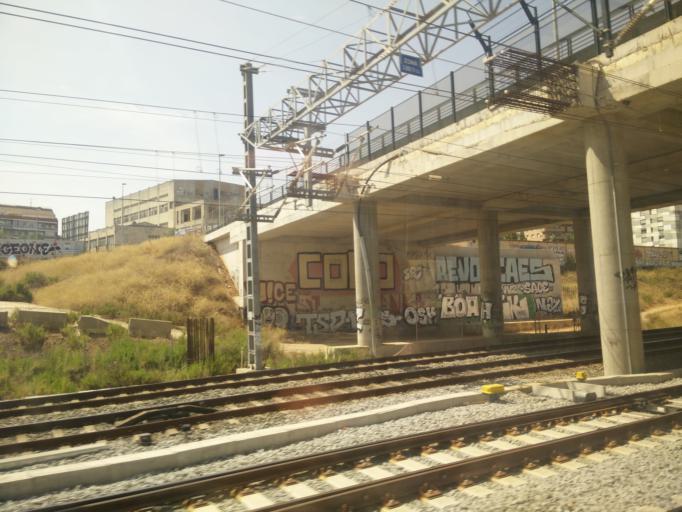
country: ES
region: Catalonia
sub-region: Provincia de Barcelona
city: Sant Marti
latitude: 41.4238
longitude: 2.1942
